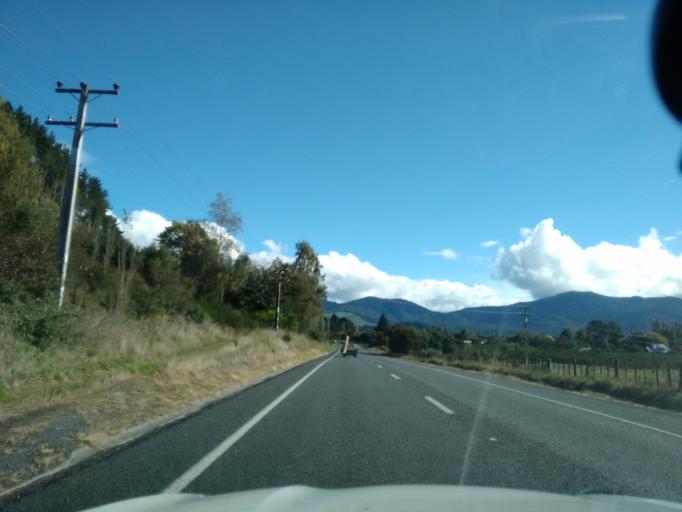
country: NZ
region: Waikato
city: Turangi
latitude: -38.9813
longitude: 175.8236
